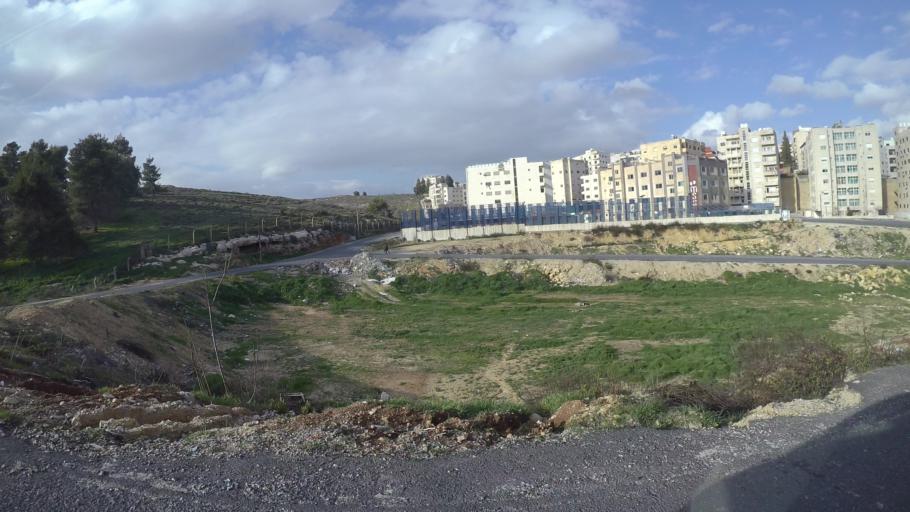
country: JO
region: Amman
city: Al Jubayhah
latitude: 32.0090
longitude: 35.8597
